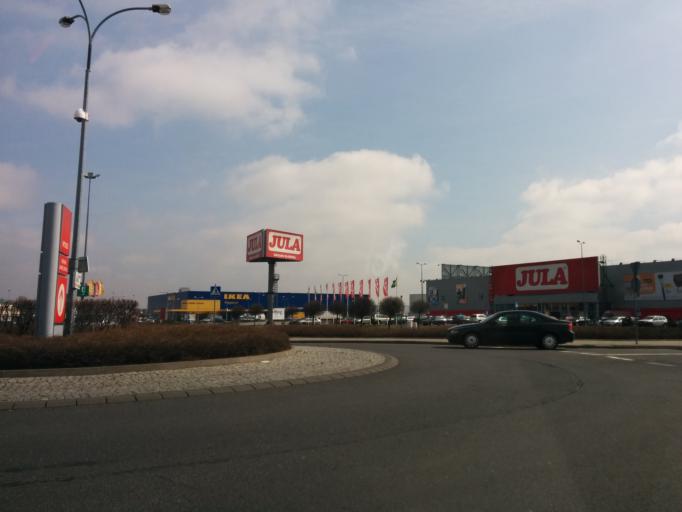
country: PL
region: Masovian Voivodeship
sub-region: Powiat wolominski
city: Zabki
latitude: 52.3041
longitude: 21.0803
